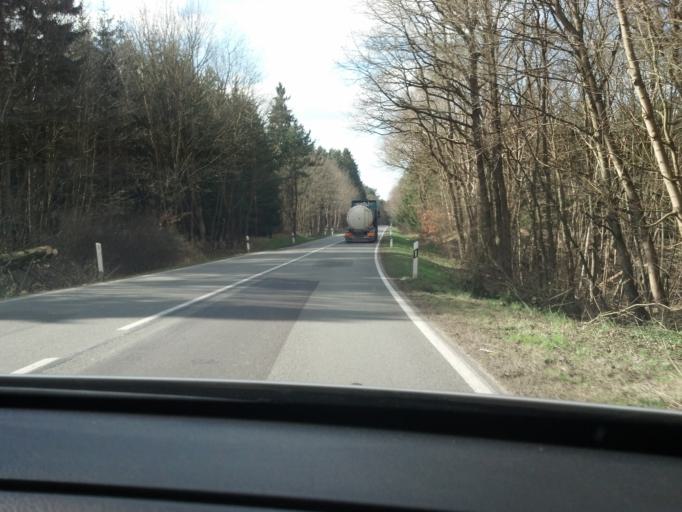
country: DE
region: Mecklenburg-Vorpommern
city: Plau am See
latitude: 53.3851
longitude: 12.3093
